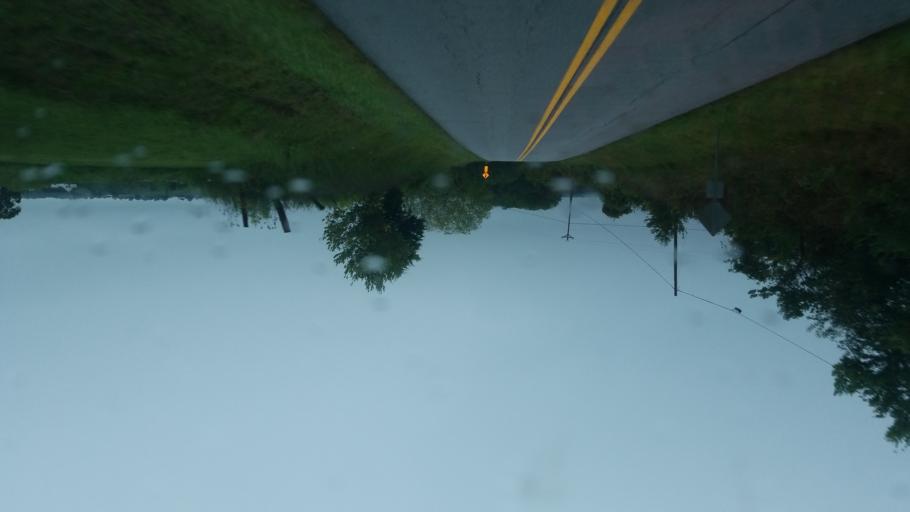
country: US
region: Kentucky
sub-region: Fleming County
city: Flemingsburg
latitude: 38.4136
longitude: -83.6838
